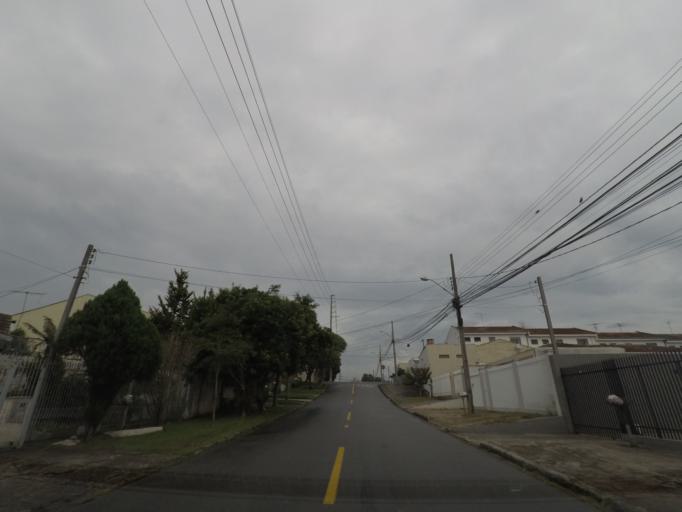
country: BR
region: Parana
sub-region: Curitiba
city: Curitiba
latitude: -25.4679
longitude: -49.3087
